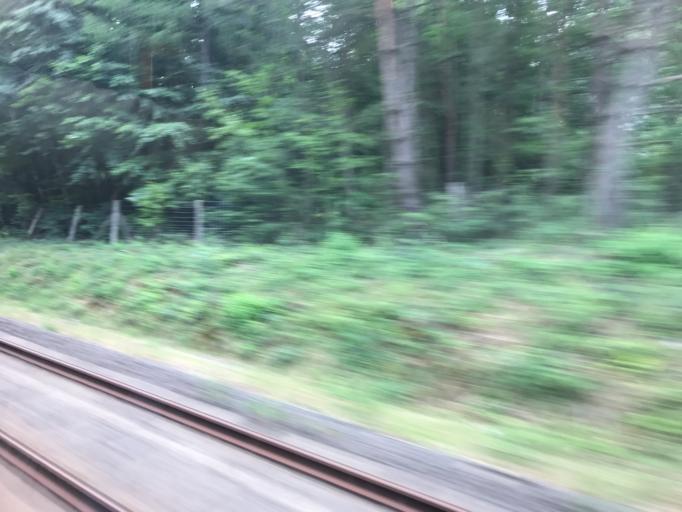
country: DE
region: Hesse
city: Niederrad
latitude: 50.0631
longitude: 8.5895
